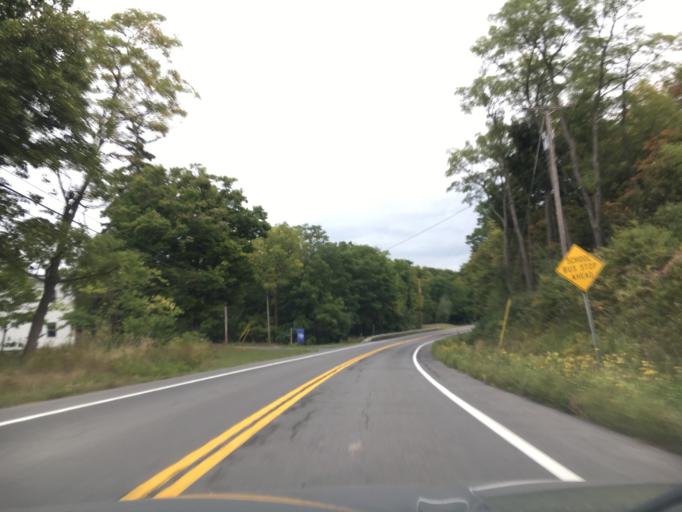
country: US
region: New York
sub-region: Tompkins County
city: Trumansburg
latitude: 42.6693
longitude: -76.7309
